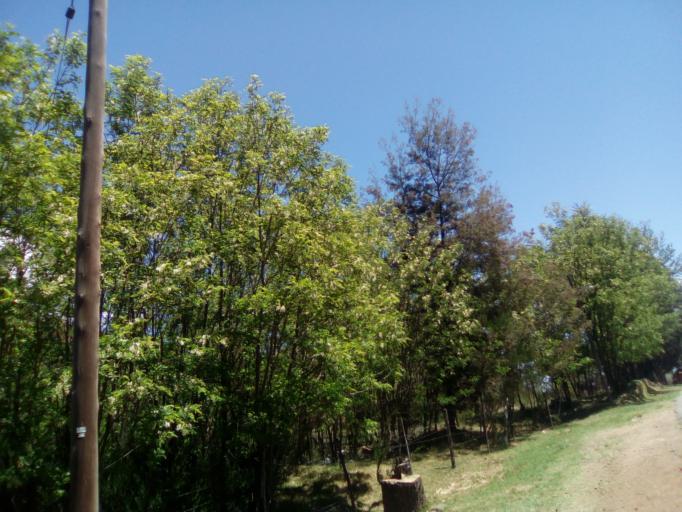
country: LS
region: Qacha's Nek
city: Qacha's Nek
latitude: -30.1209
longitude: 28.6892
